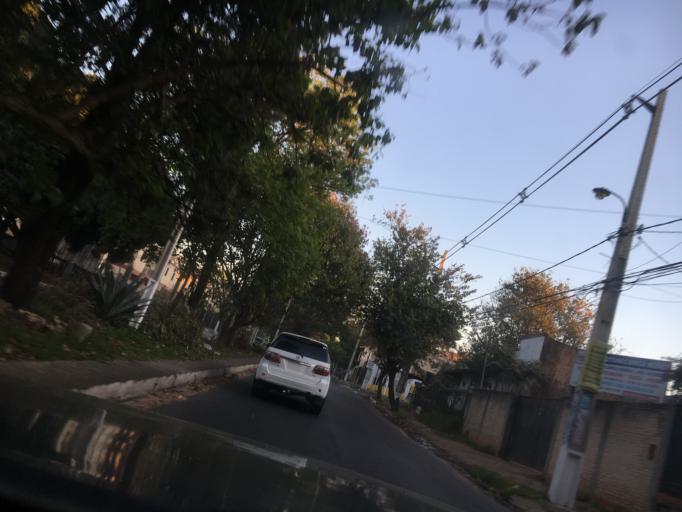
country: PY
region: Central
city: Lambare
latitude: -25.3358
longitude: -57.6069
